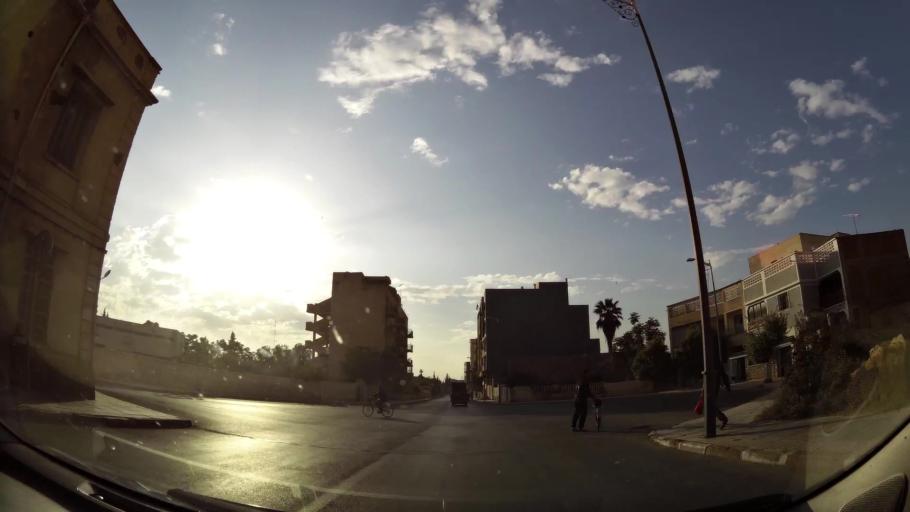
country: MA
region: Oriental
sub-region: Oujda-Angad
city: Oujda
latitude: 34.6747
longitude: -1.9220
